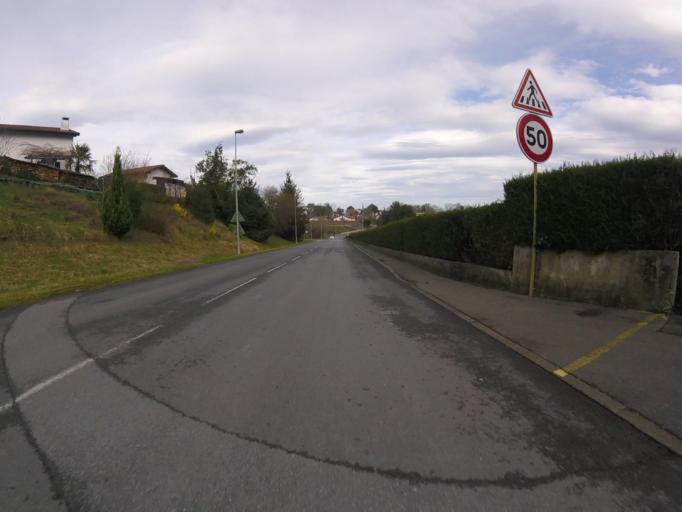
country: FR
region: Aquitaine
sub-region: Departement des Pyrenees-Atlantiques
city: Saint-Jean-de-Luz
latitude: 43.3717
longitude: -1.6590
